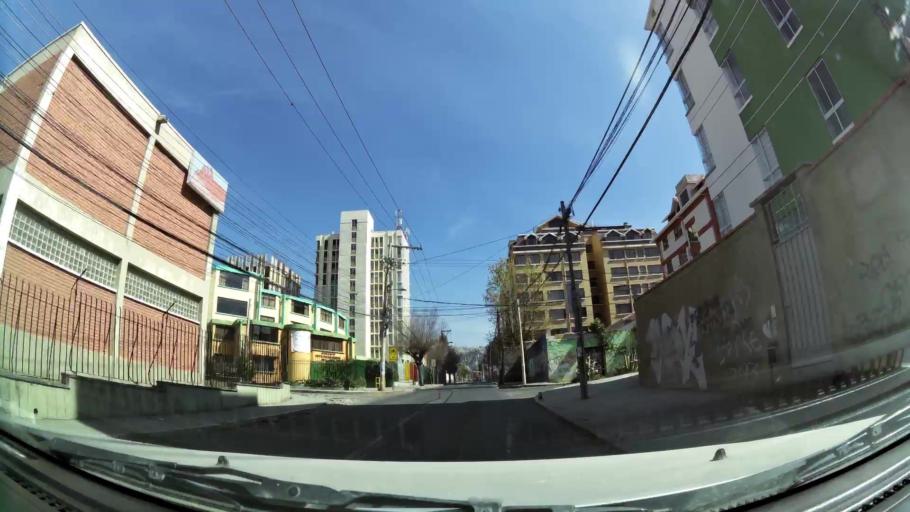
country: BO
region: La Paz
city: La Paz
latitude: -16.5288
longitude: -68.1049
